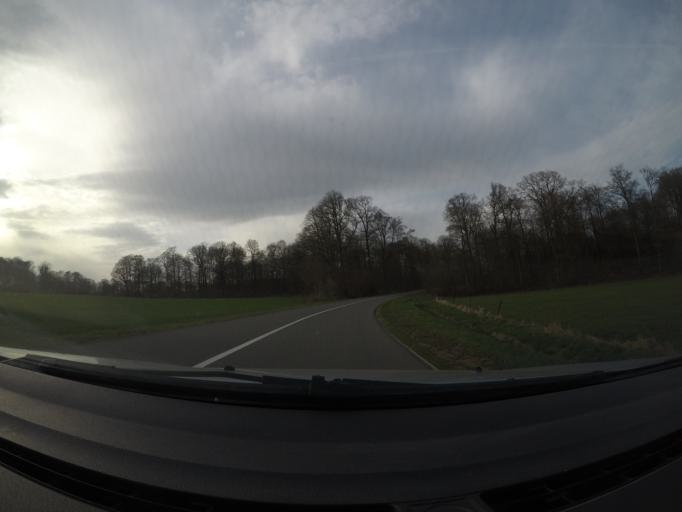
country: BE
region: Wallonia
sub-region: Province du Luxembourg
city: Messancy
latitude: 49.6140
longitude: 5.8446
